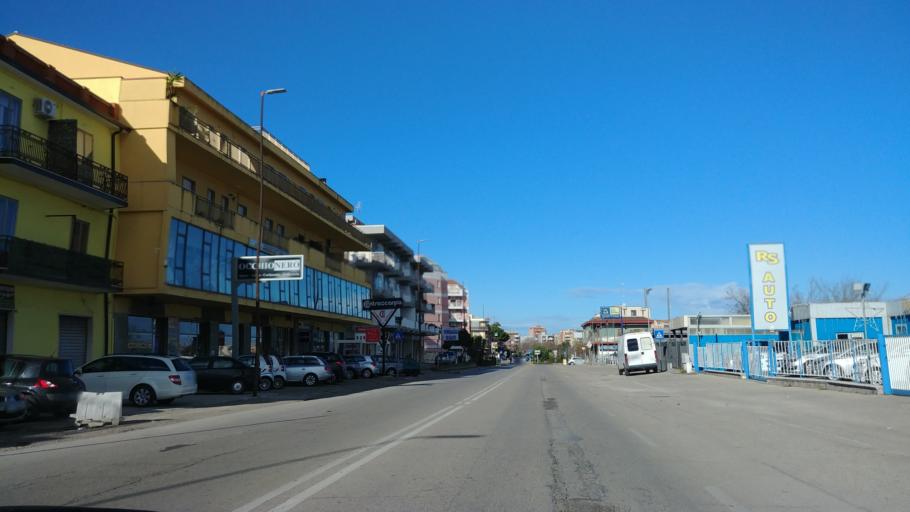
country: IT
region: Molise
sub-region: Provincia di Campobasso
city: Termoli
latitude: 41.9917
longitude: 14.9995
